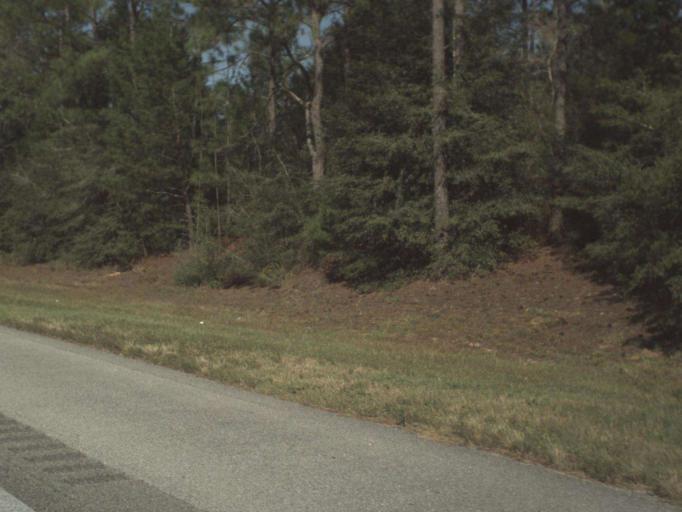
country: US
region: Florida
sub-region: Okaloosa County
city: Crestview
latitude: 30.7269
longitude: -86.4981
